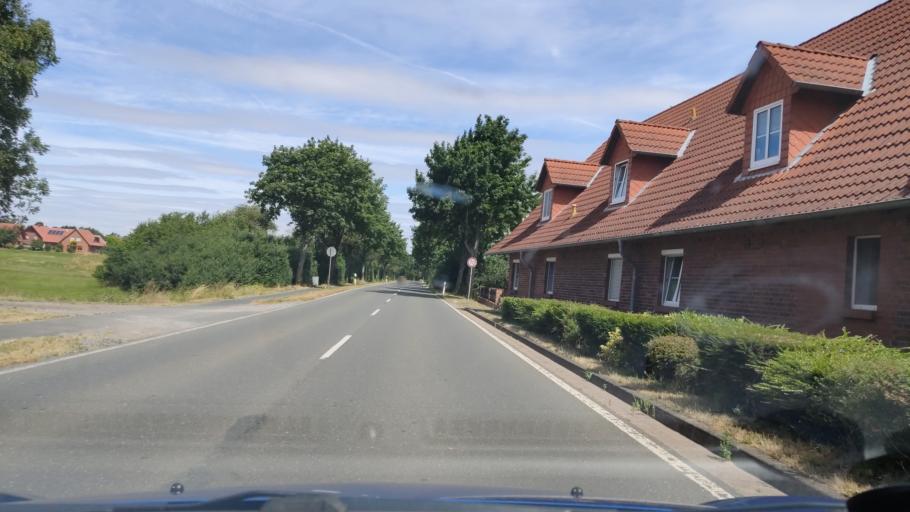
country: DE
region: Lower Saxony
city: Neustadt am Rubenberge
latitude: 52.5313
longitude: 9.4635
